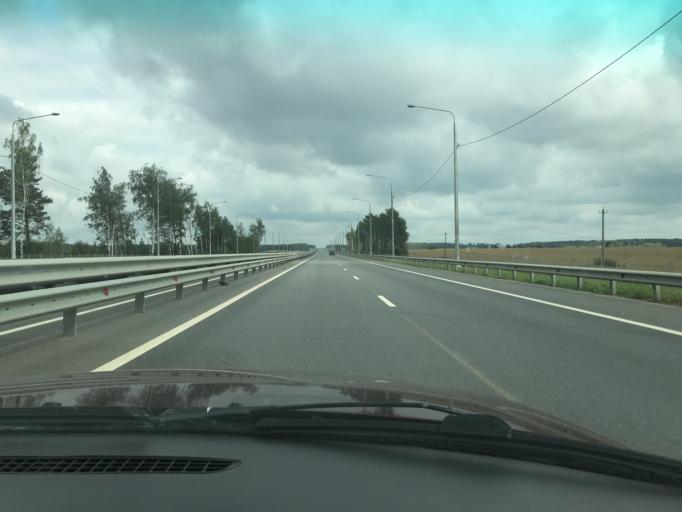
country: RU
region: Kaluga
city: Detchino
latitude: 54.7586
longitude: 36.2157
